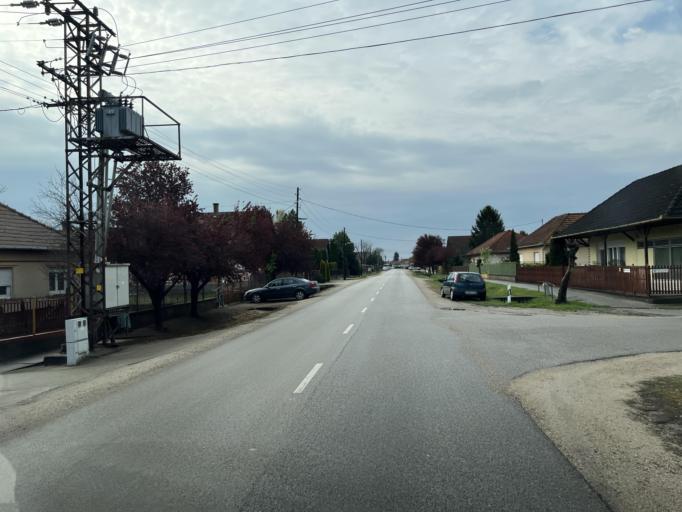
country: HU
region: Pest
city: Nyaregyhaza
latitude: 47.2335
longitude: 19.4472
